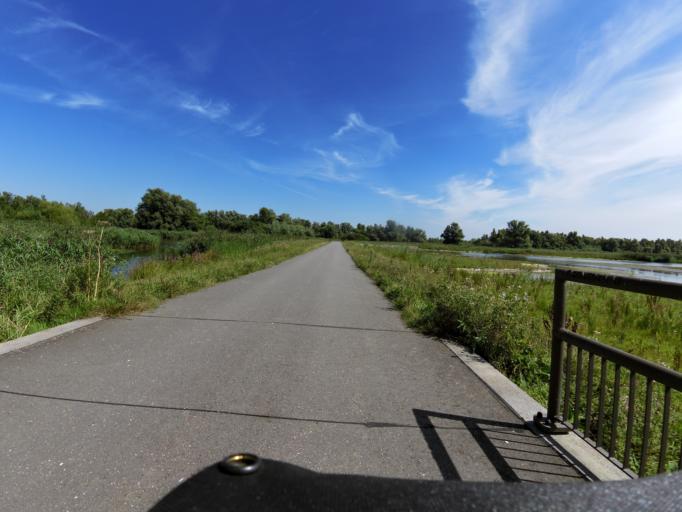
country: NL
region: South Holland
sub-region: Gemeente Sliedrecht
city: Sliedrecht
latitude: 51.7752
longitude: 4.7633
